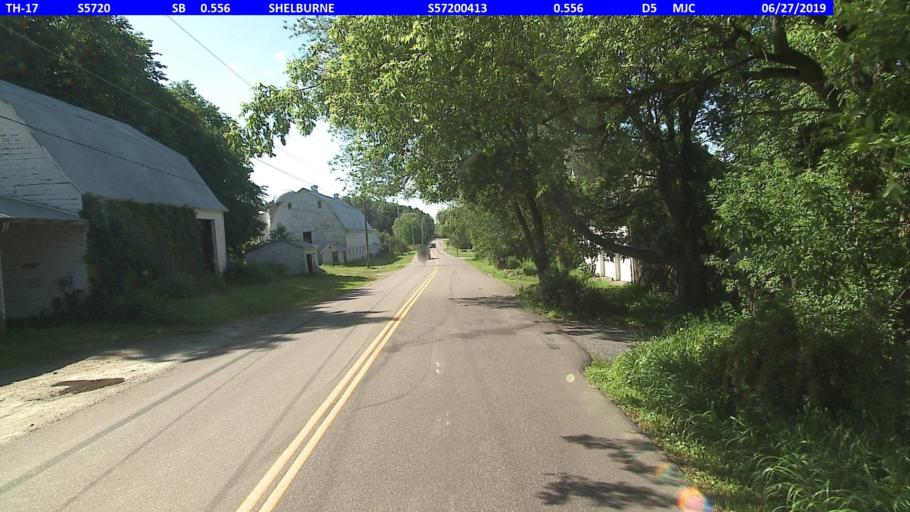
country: US
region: Vermont
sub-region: Chittenden County
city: Hinesburg
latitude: 44.3659
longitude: -73.2008
